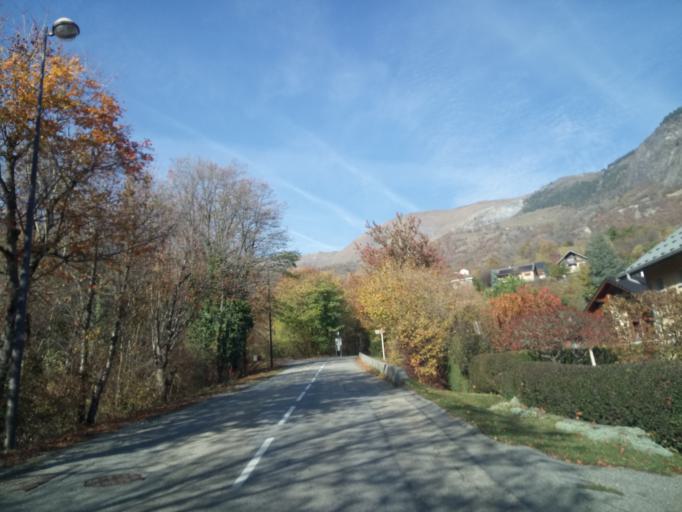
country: FR
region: Rhone-Alpes
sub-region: Departement de la Savoie
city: Saint-Jean-de-Maurienne
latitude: 45.2714
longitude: 6.3387
